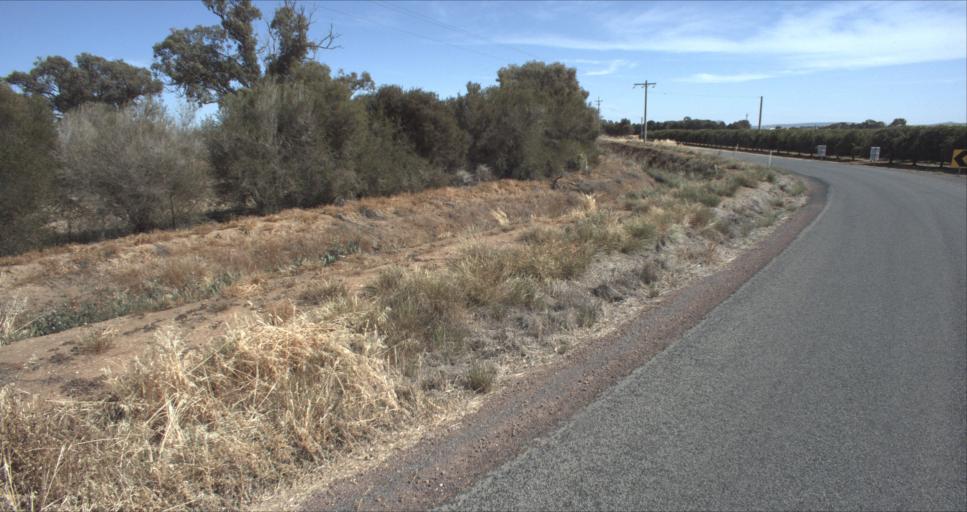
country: AU
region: New South Wales
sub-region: Leeton
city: Leeton
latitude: -34.5751
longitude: 146.4676
